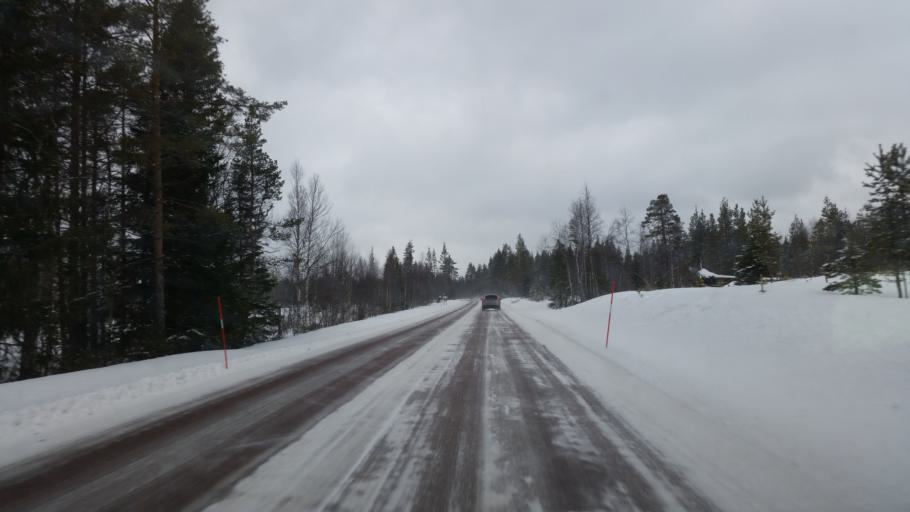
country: SE
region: Jaemtland
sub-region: Bergs Kommun
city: Hoverberg
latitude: 62.4123
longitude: 14.6192
